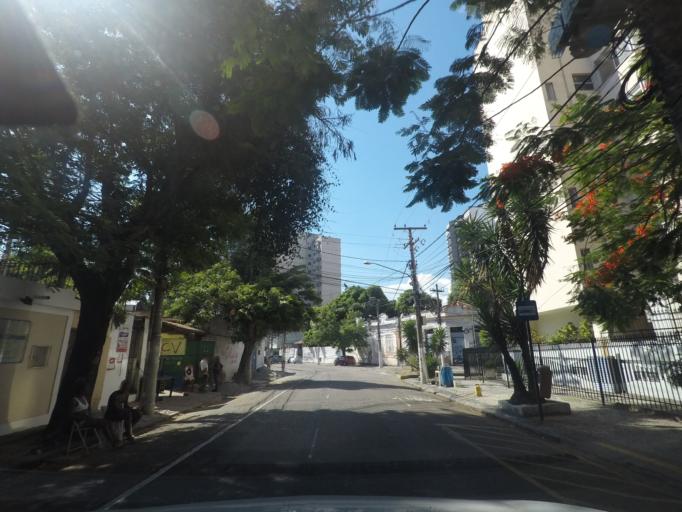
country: BR
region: Rio de Janeiro
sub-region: Niteroi
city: Niteroi
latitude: -22.9006
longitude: -43.1280
